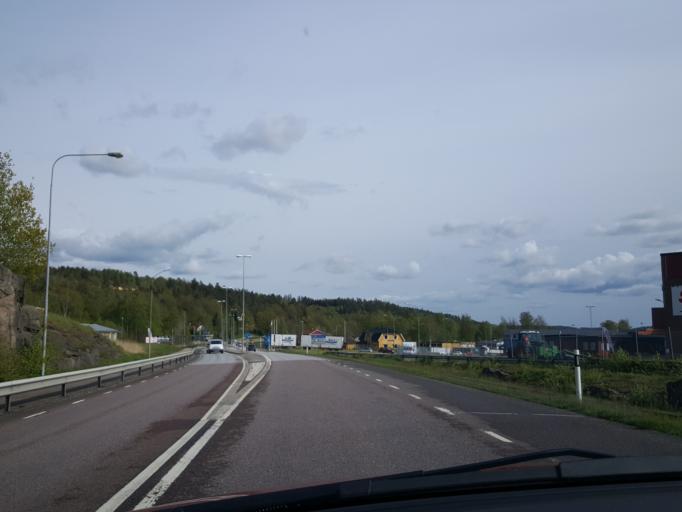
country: SE
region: Vaestra Goetaland
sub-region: Lilla Edets Kommun
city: Lilla Edet
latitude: 58.1098
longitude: 12.1447
